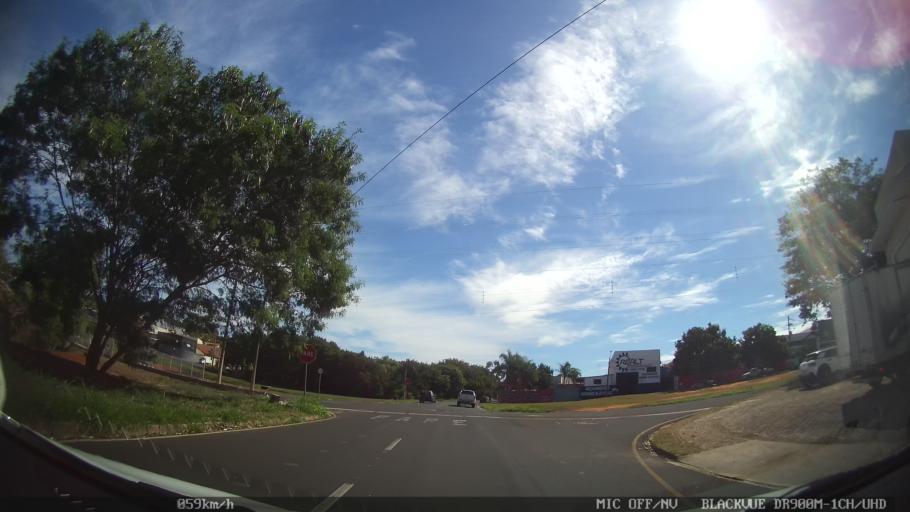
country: BR
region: Sao Paulo
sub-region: Sao Jose Do Rio Preto
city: Sao Jose do Rio Preto
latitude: -20.8423
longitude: -49.3617
